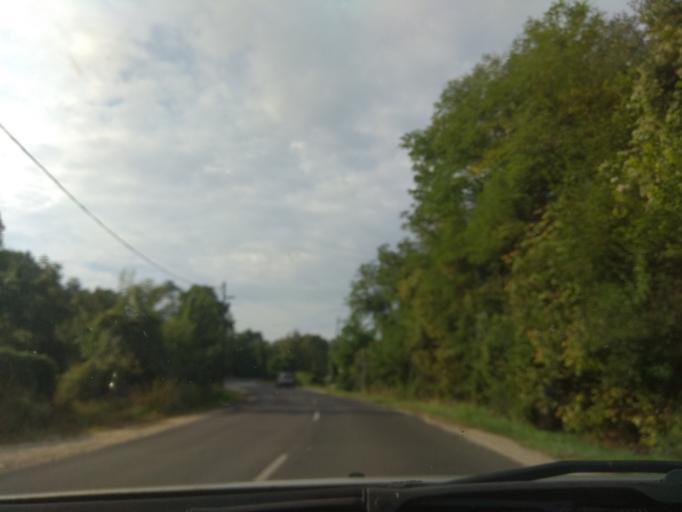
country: HU
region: Borsod-Abauj-Zemplen
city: Miskolc
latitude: 48.0880
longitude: 20.7522
